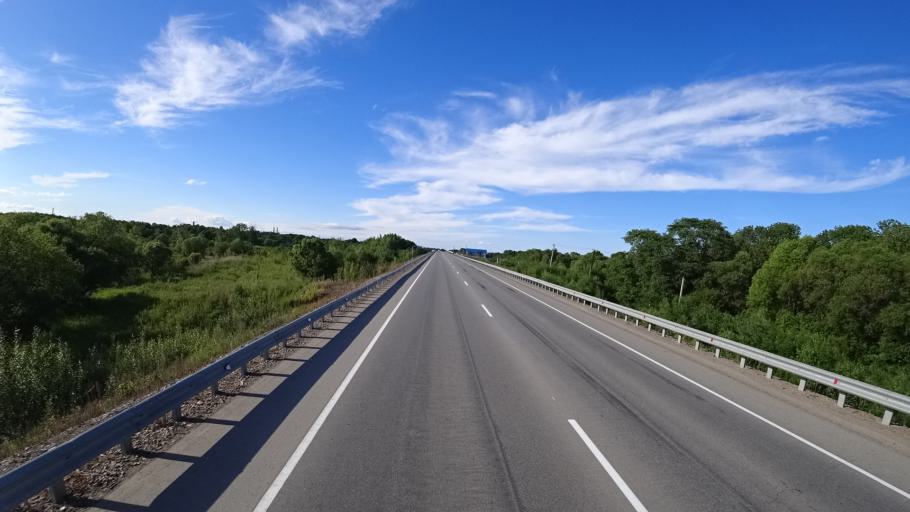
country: RU
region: Khabarovsk Krai
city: Khor
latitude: 47.8608
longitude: 134.9630
